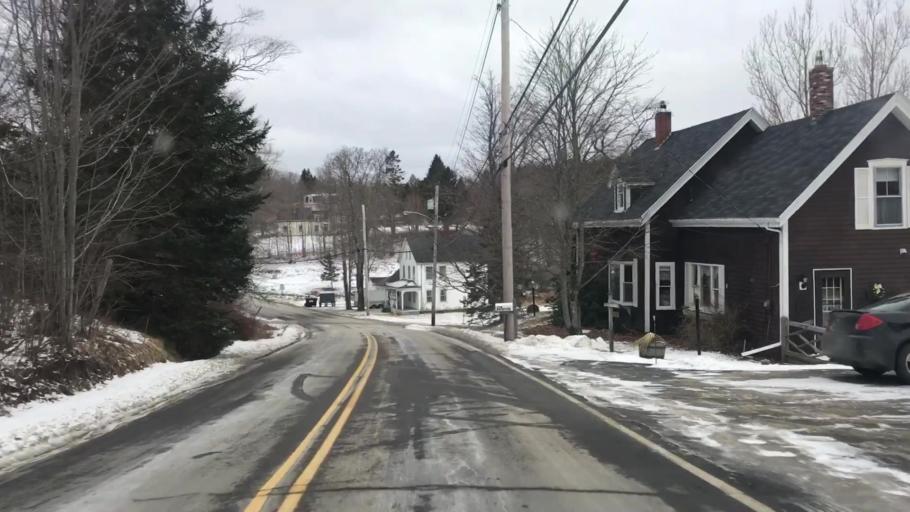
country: US
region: Maine
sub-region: Washington County
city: East Machias
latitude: 44.7329
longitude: -67.3900
